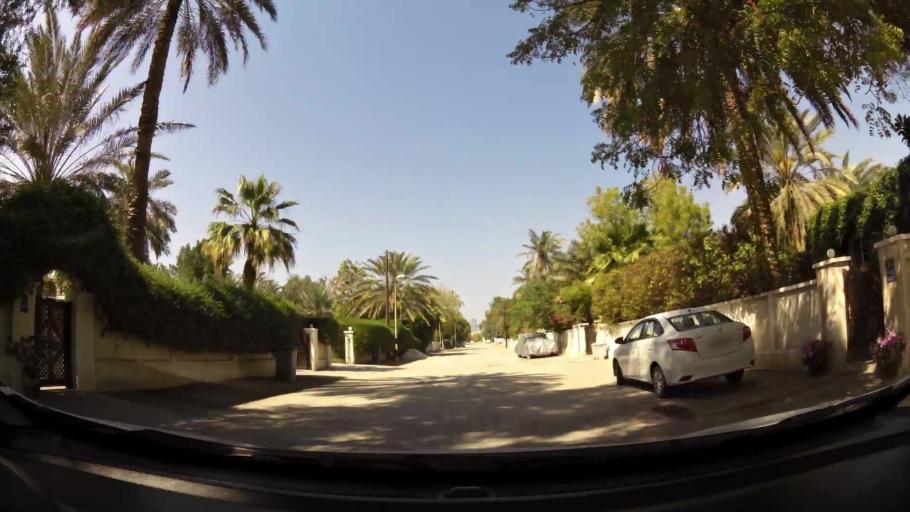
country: BH
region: Manama
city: Manama
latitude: 26.2149
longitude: 50.5834
